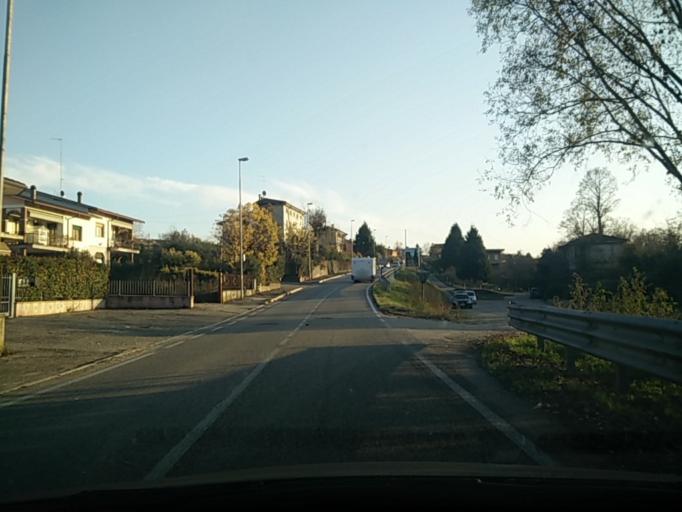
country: IT
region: Veneto
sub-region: Provincia di Verona
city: Salionze
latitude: 45.4093
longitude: 10.7192
